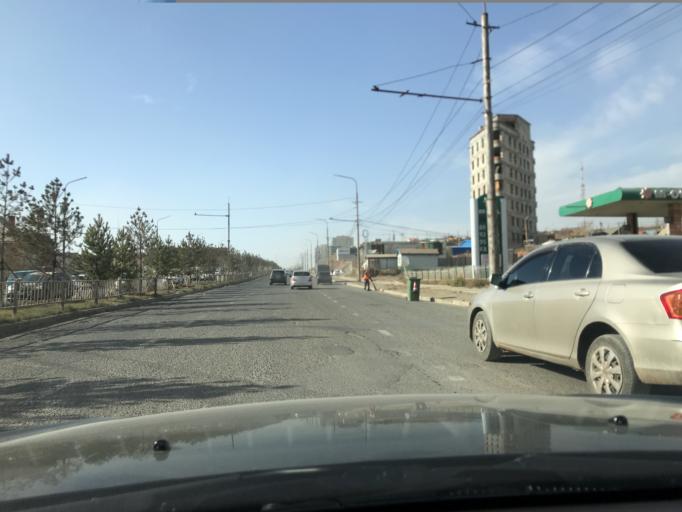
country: MN
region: Ulaanbaatar
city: Ulaanbaatar
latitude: 47.9276
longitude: 106.9036
